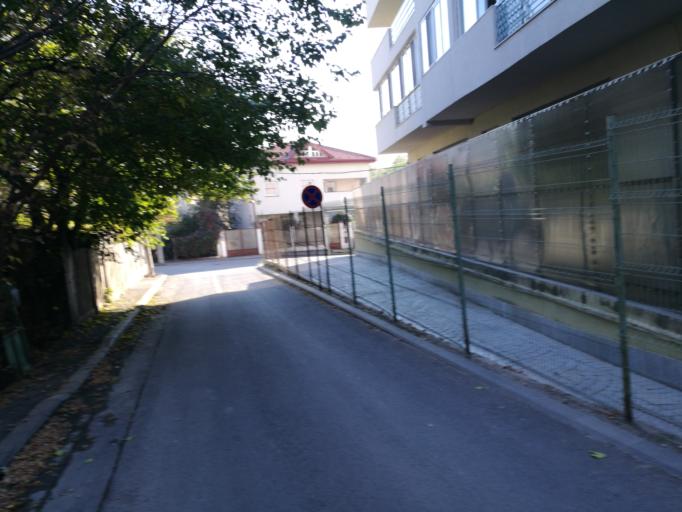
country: RO
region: Bucuresti
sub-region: Municipiul Bucuresti
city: Bucharest
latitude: 44.4796
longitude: 26.0889
